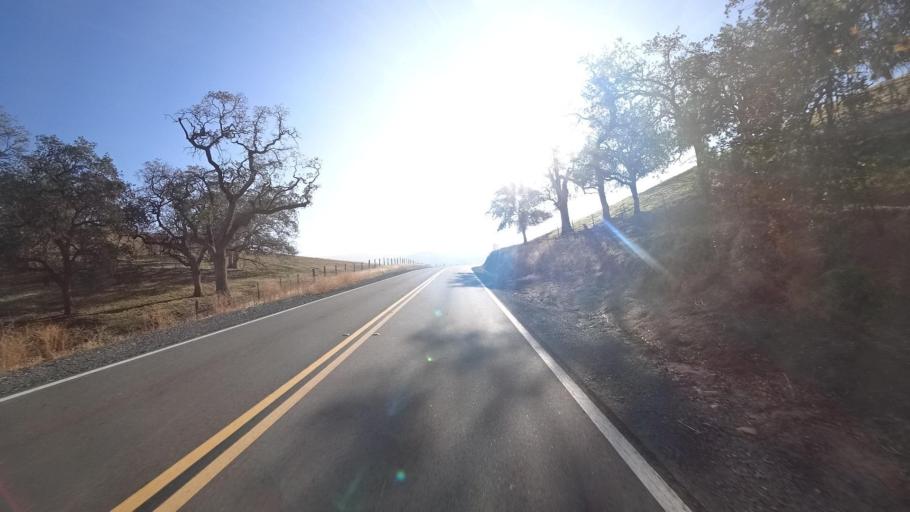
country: US
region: California
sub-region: Tulare County
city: Richgrove
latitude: 35.7130
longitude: -118.8456
